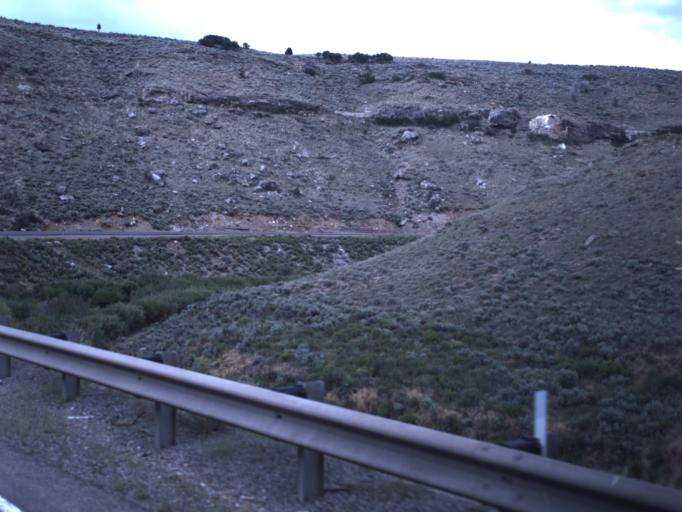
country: US
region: Utah
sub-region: Carbon County
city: Helper
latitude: 39.7876
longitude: -110.7918
